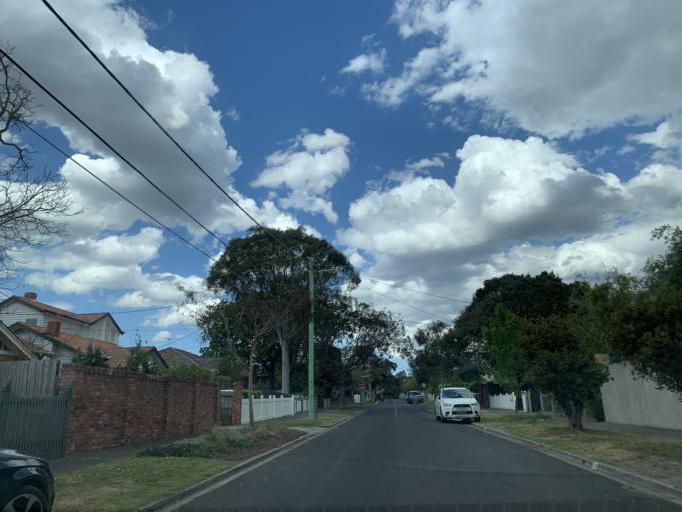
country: AU
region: Victoria
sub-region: Bayside
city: Hampton
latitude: -37.9406
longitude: 145.0139
